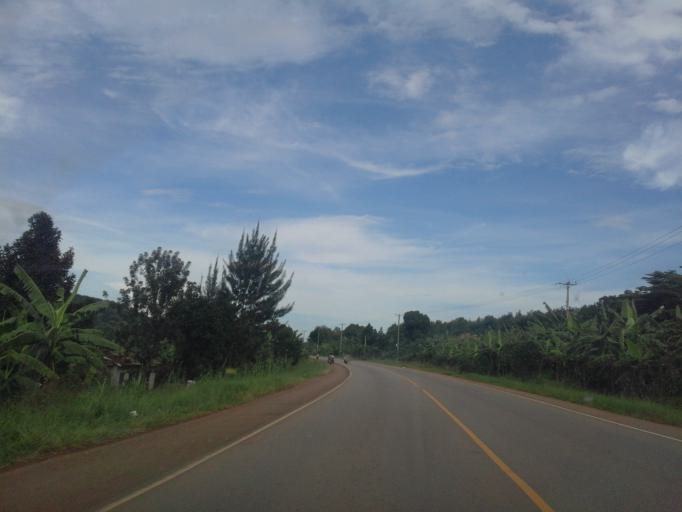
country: UG
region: Central Region
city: Masaka
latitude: -0.3425
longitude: 31.6338
